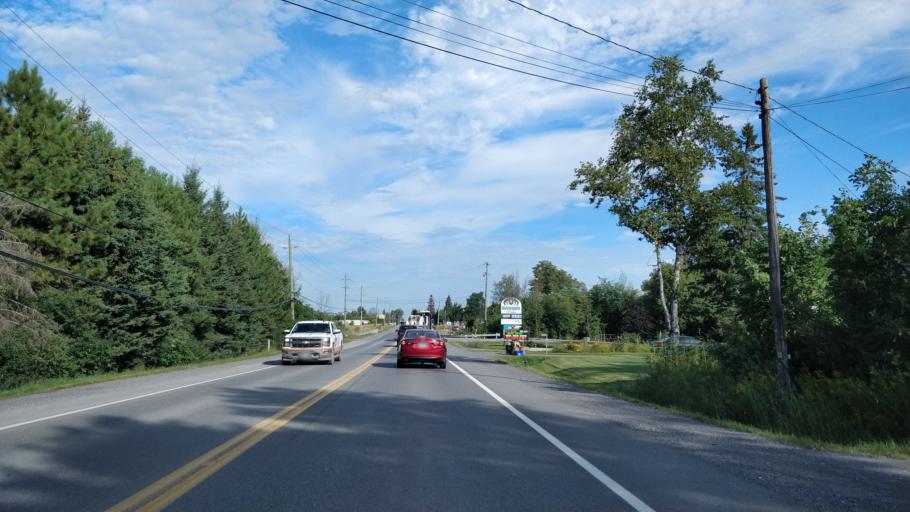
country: CA
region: Ontario
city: Bells Corners
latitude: 45.2987
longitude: -75.9788
